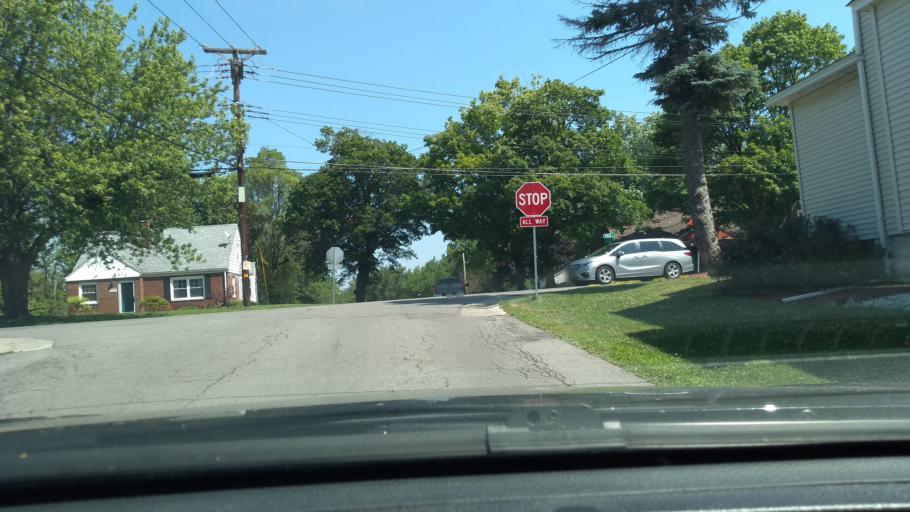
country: US
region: New York
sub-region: Erie County
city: West Seneca
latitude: 42.8324
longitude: -78.7592
